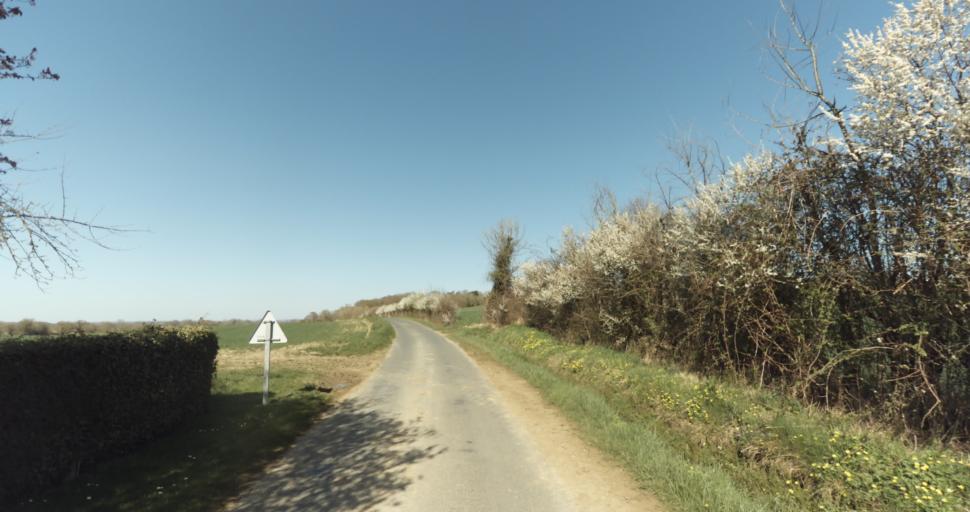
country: FR
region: Lower Normandy
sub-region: Departement du Calvados
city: Saint-Pierre-sur-Dives
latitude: 48.9478
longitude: -0.0049
